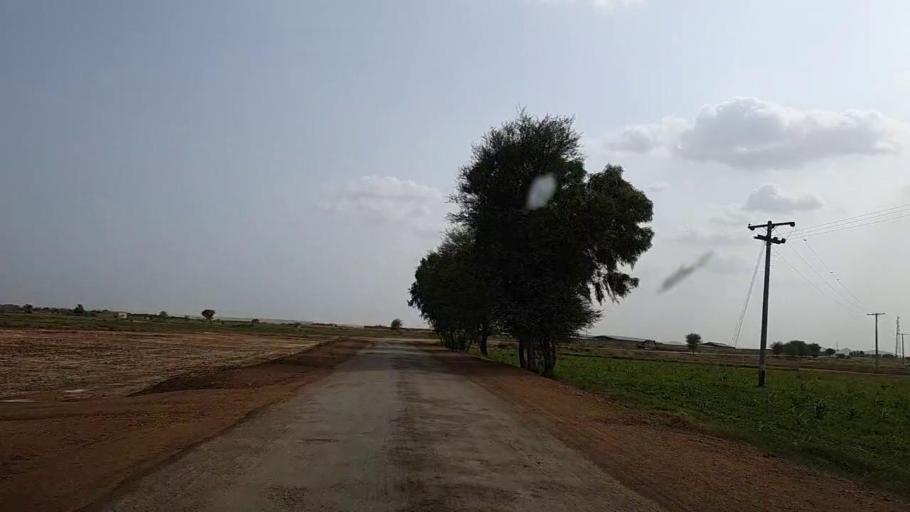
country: PK
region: Sindh
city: Kotri
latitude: 25.2538
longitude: 68.2400
